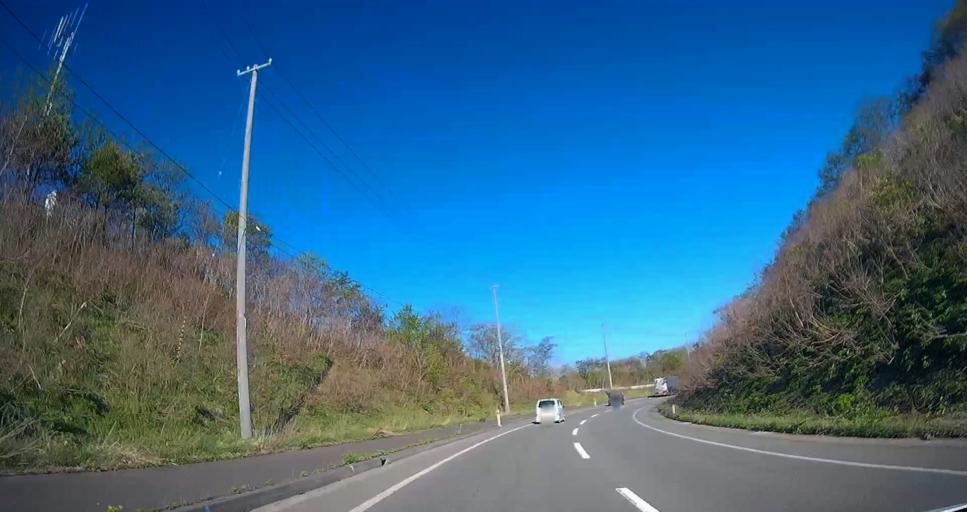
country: JP
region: Aomori
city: Mutsu
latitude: 41.4307
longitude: 141.1440
